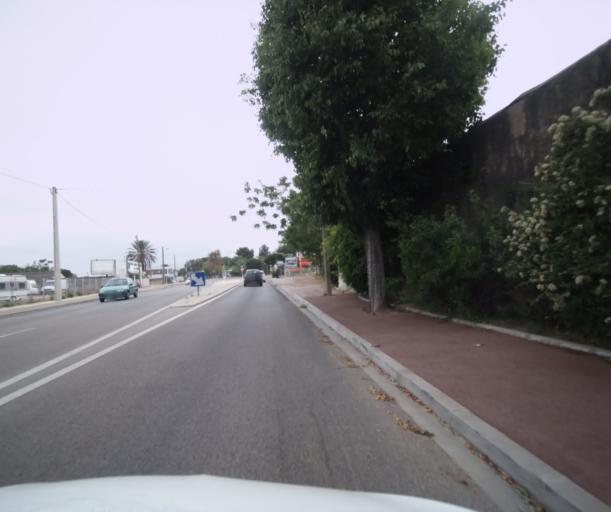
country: FR
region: Provence-Alpes-Cote d'Azur
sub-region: Departement du Var
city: La Seyne-sur-Mer
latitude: 43.1220
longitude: 5.8943
